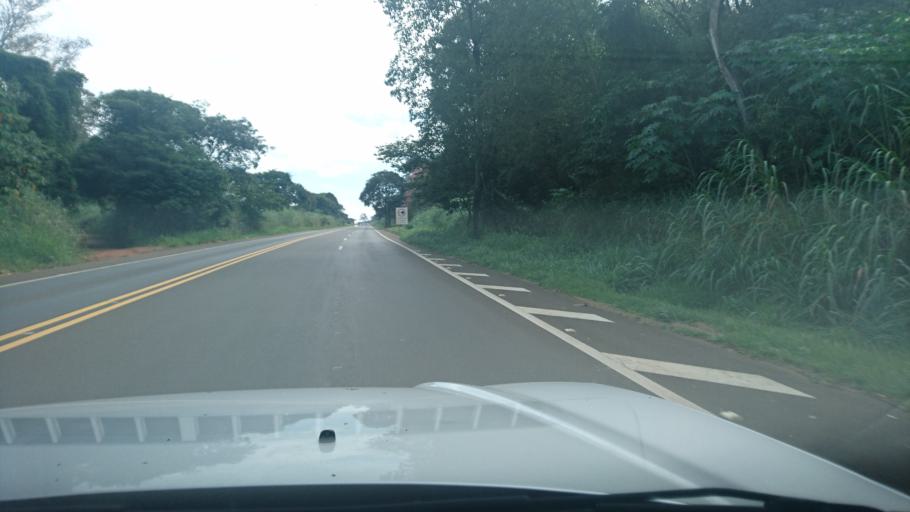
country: BR
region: Sao Paulo
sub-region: Pirassununga
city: Pirassununga
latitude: -22.0449
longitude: -47.4478
